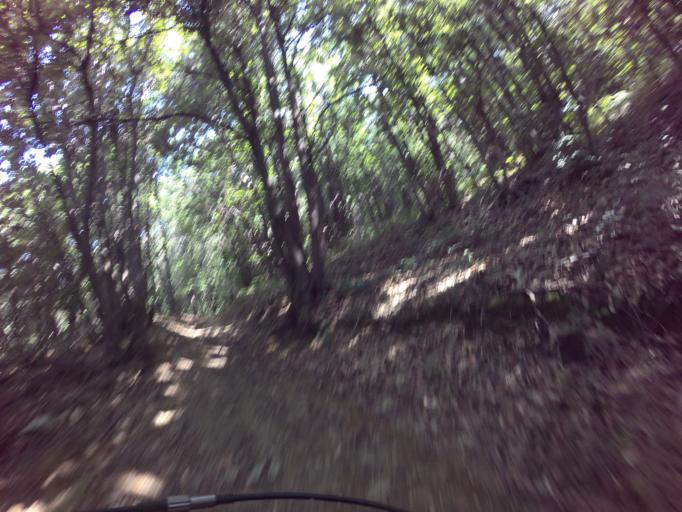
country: IT
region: Piedmont
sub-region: Provincia di Cuneo
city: Roccaforte Mondovi
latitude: 44.3277
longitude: 7.7127
